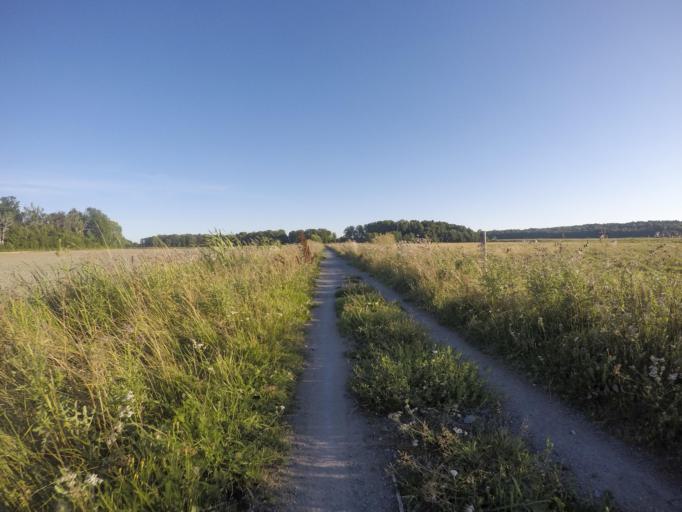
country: SE
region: Vaestmanland
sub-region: Vasteras
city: Vasteras
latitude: 59.5611
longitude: 16.6492
